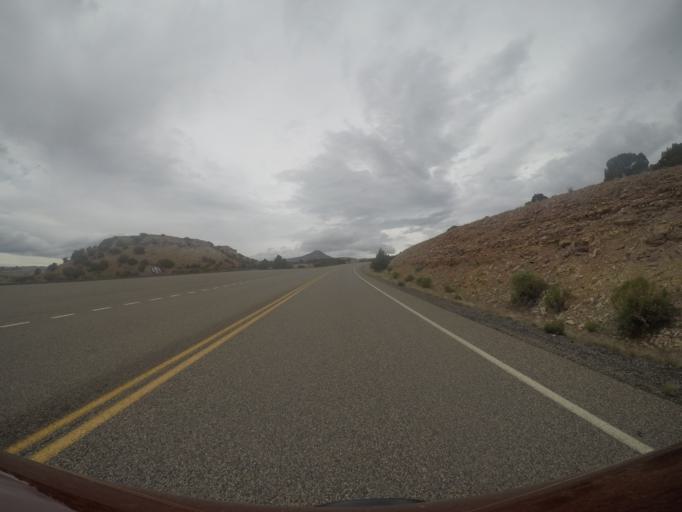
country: US
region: Wyoming
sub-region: Big Horn County
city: Lovell
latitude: 44.9866
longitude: -108.2614
